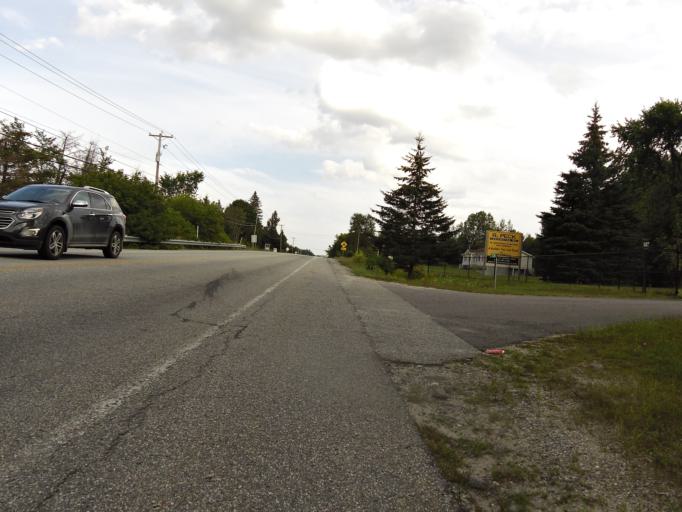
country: CA
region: Quebec
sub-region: Outaouais
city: Wakefield
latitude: 45.6219
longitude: -75.9301
